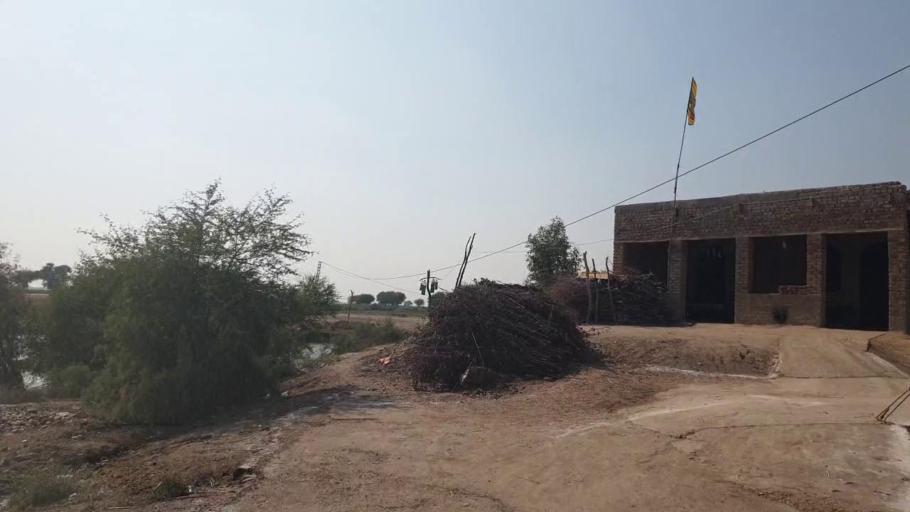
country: PK
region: Sindh
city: Sehwan
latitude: 26.4223
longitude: 67.8281
